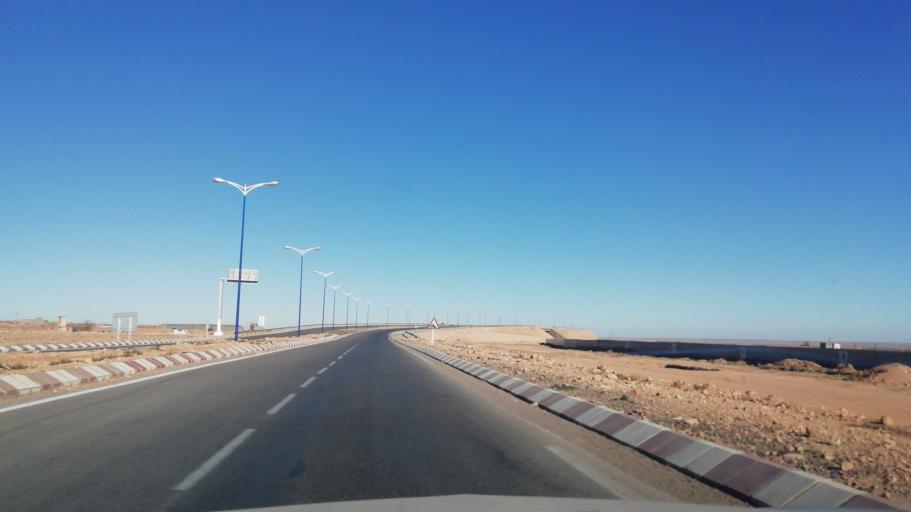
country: DZ
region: Wilaya de Naama
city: Naama
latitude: 33.5114
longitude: -0.2855
